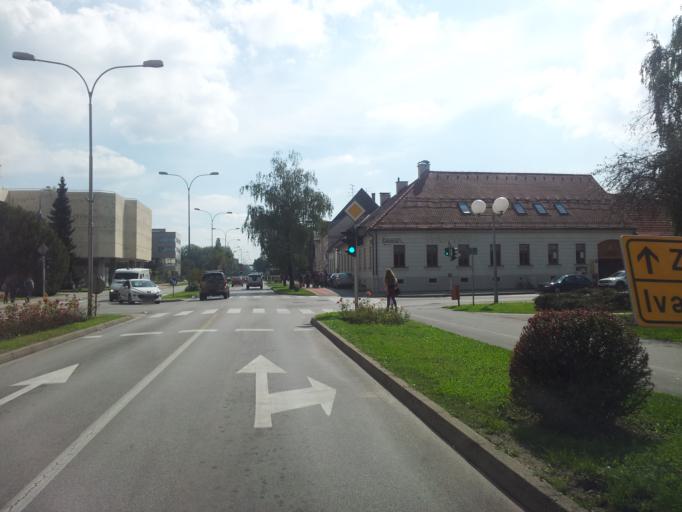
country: HR
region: Varazdinska
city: Varazdin
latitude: 46.3068
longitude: 16.3337
